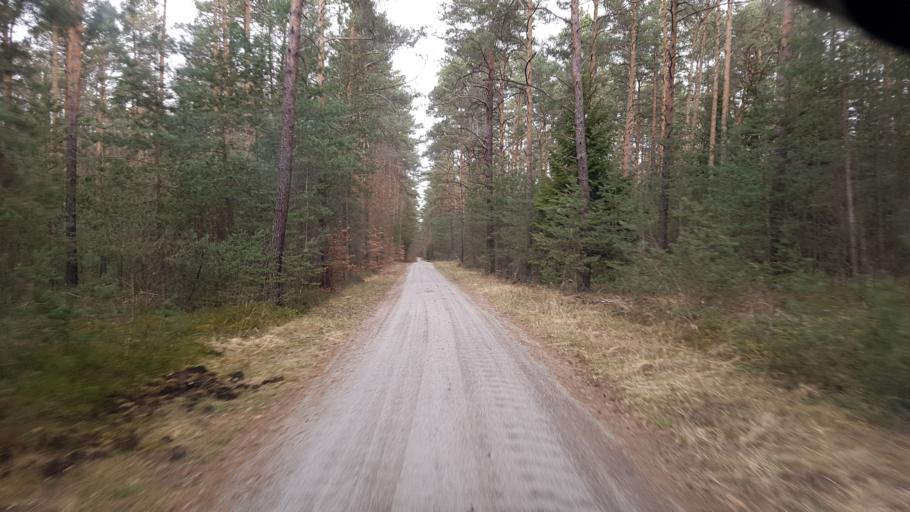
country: DE
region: Brandenburg
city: Finsterwalde
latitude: 51.5706
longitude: 13.7050
